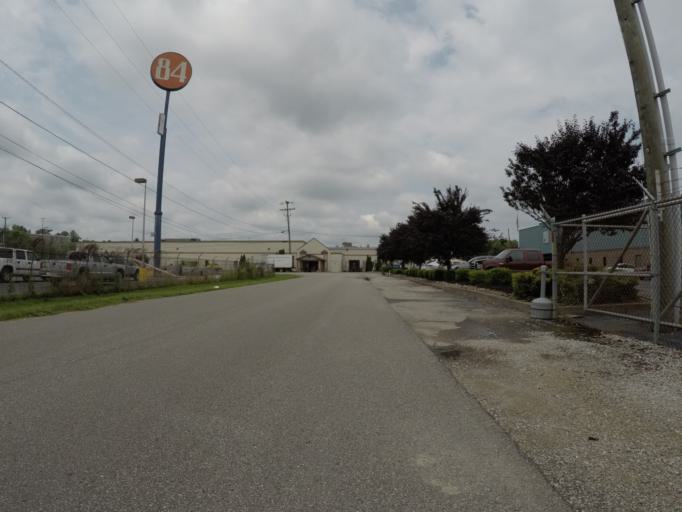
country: US
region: West Virginia
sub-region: Cabell County
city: Pea Ridge
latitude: 38.4156
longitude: -82.3434
